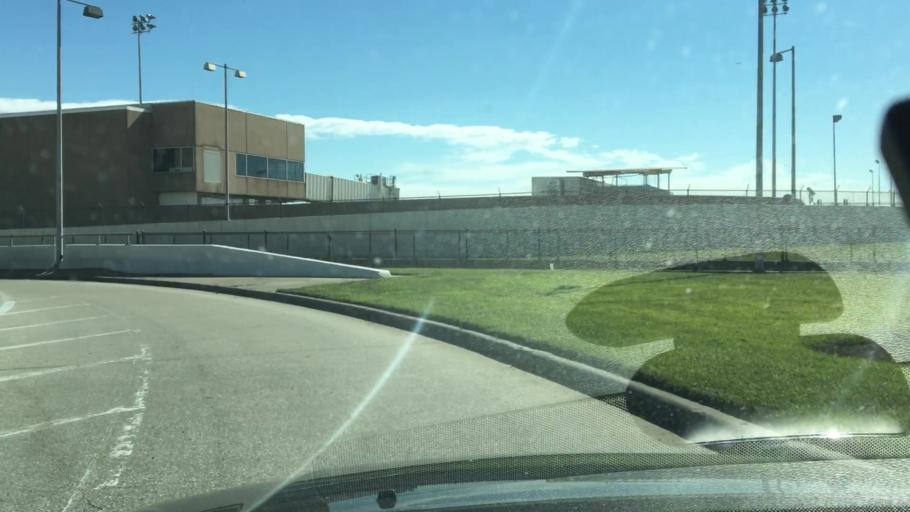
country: US
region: Texas
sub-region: Harris County
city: Aldine
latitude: 29.9859
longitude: -95.3409
